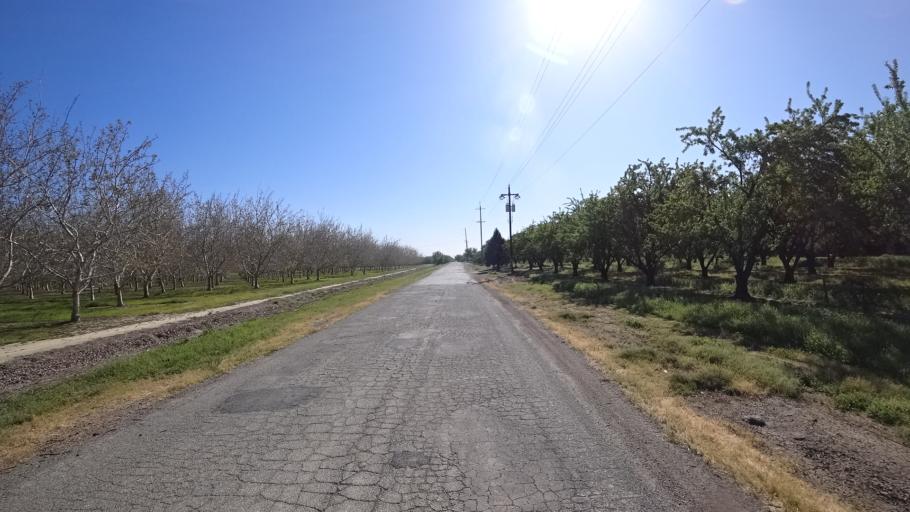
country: US
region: California
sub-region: Glenn County
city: Hamilton City
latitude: 39.7129
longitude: -122.0005
